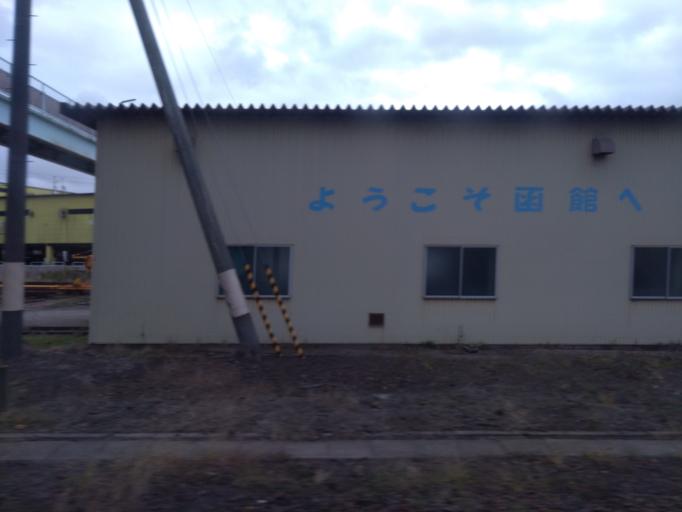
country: JP
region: Hokkaido
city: Hakodate
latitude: 41.8051
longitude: 140.7332
